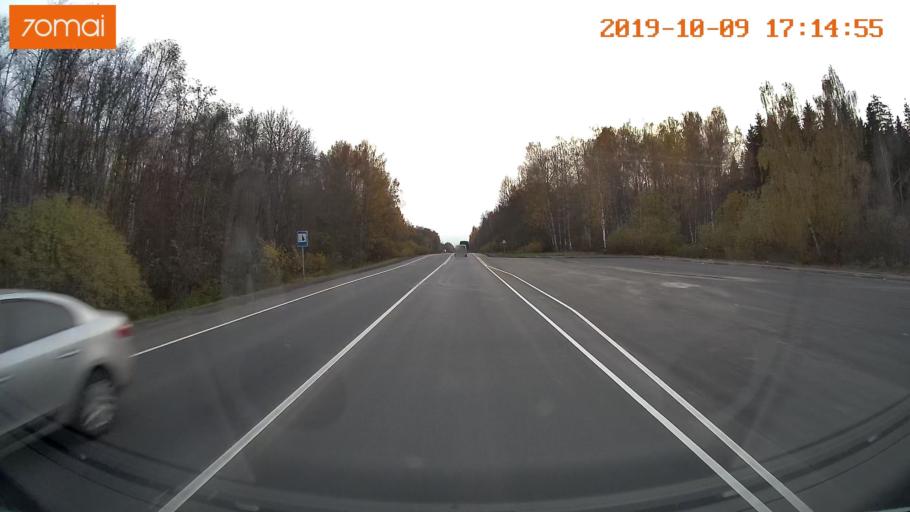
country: RU
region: Ivanovo
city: Furmanov
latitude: 57.3021
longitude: 41.2019
